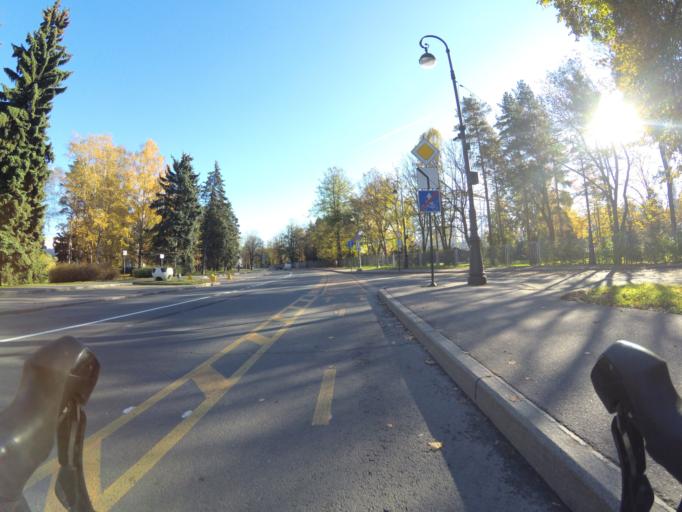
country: RU
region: Leningrad
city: Krestovskiy ostrov
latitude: 59.9741
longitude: 30.2495
